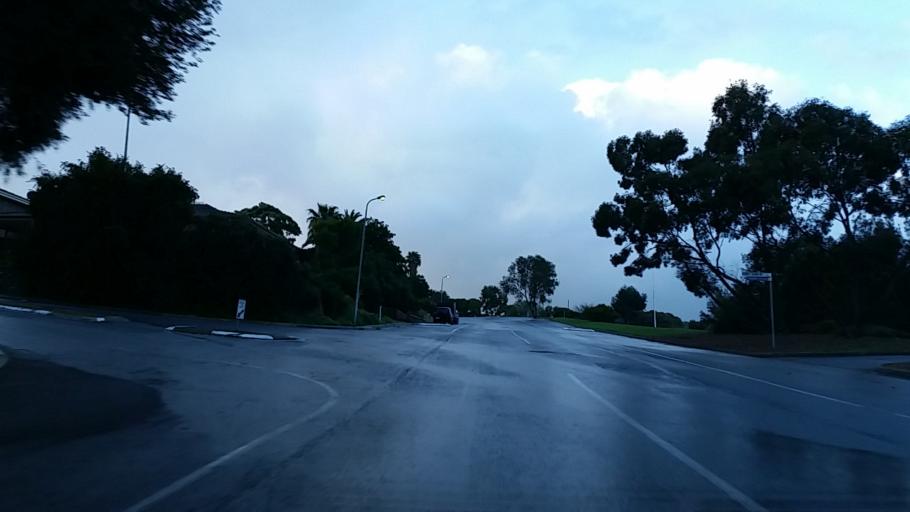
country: AU
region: South Australia
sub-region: Marion
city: Marino
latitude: -35.0703
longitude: 138.5101
